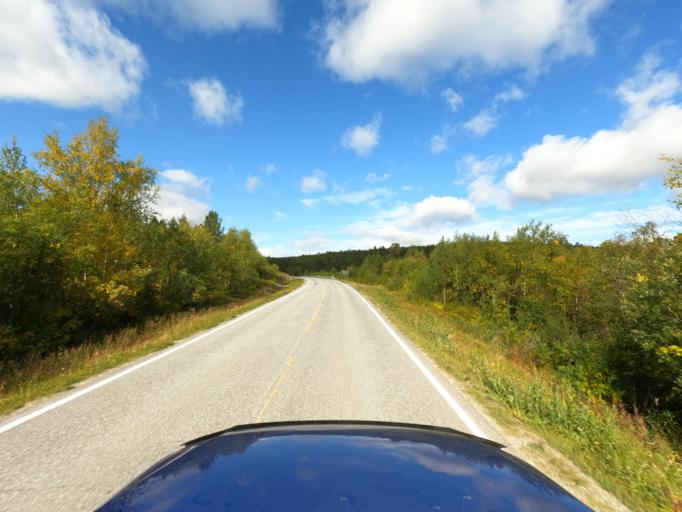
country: NO
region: Finnmark Fylke
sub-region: Karasjok
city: Karasjohka
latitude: 69.4878
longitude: 25.5041
